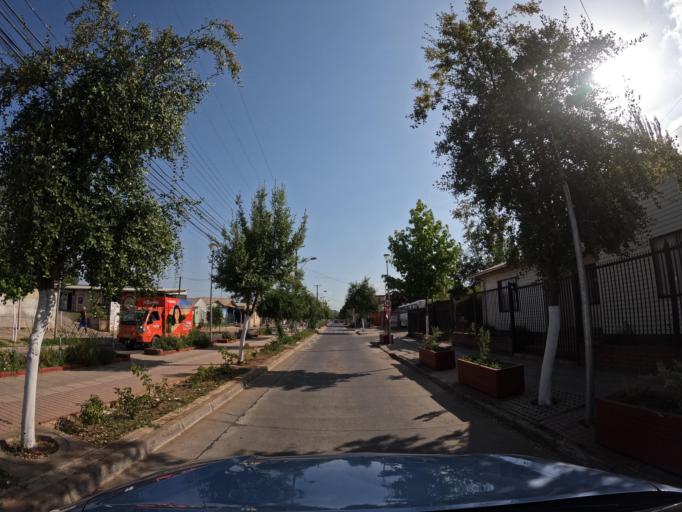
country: CL
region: Maule
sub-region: Provincia de Curico
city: Molina
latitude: -35.2820
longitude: -71.2596
